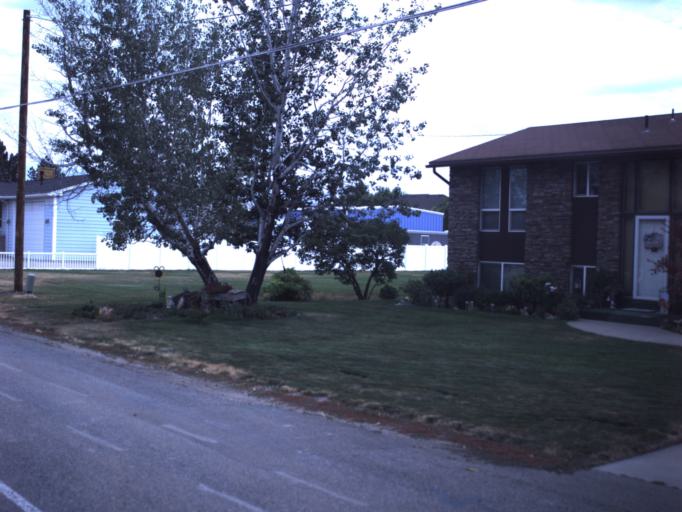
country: US
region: Utah
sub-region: Davis County
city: Syracuse
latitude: 41.0976
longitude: -112.0646
